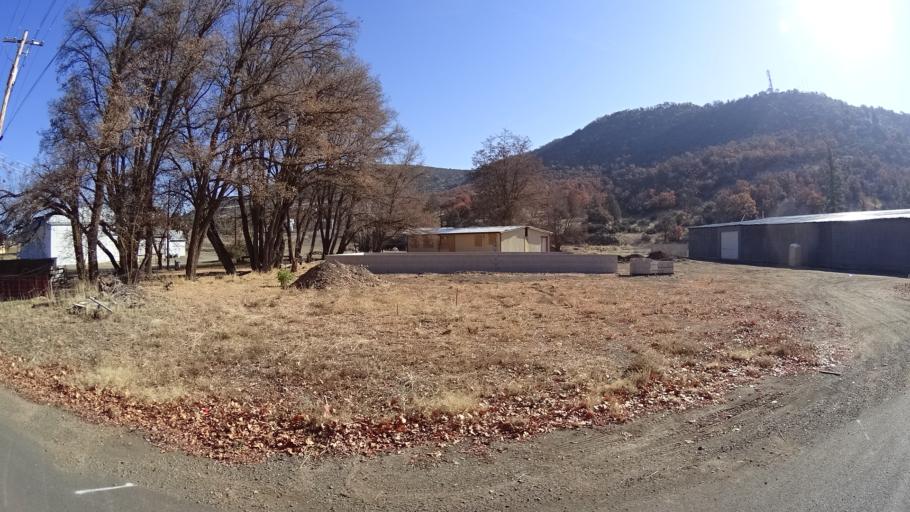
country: US
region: California
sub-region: Siskiyou County
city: Yreka
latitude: 41.7284
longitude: -122.6335
